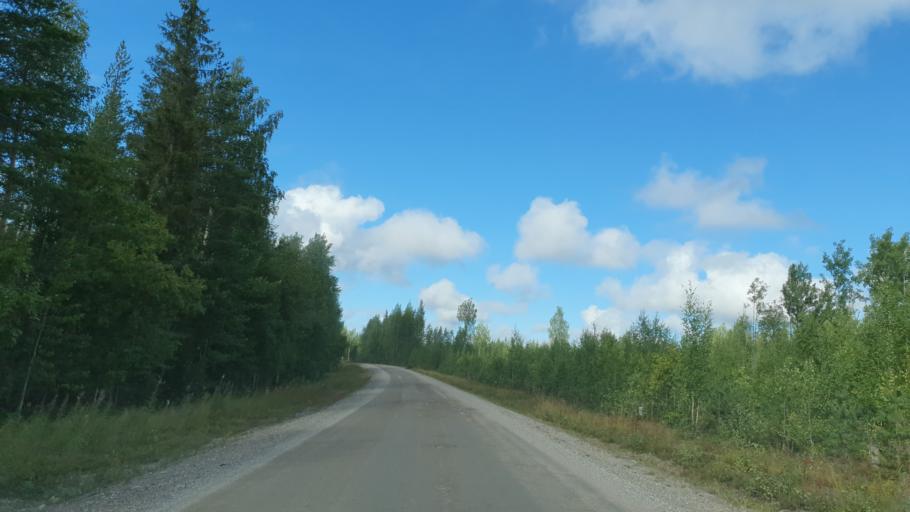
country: FI
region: Kainuu
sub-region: Kehys-Kainuu
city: Kuhmo
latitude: 63.9822
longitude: 29.2504
